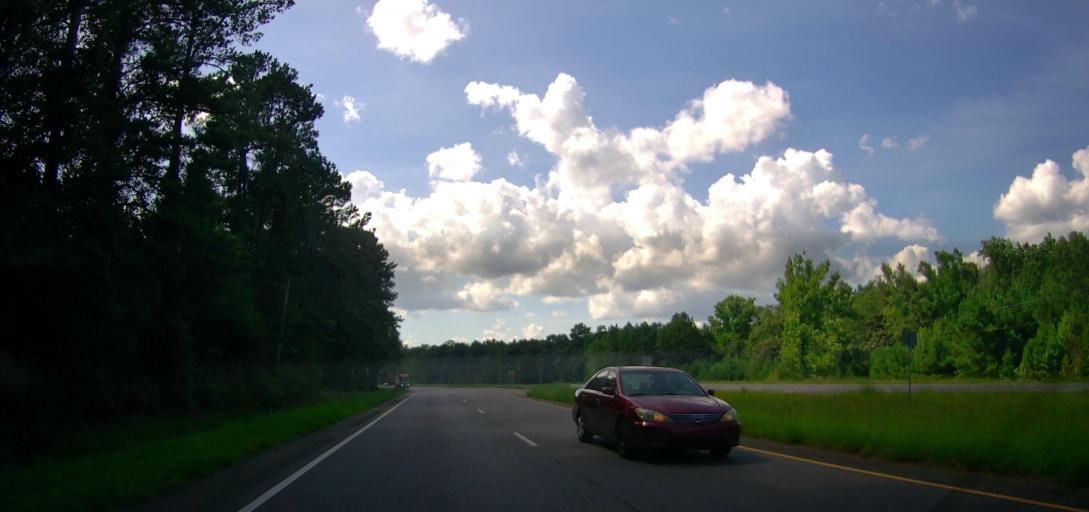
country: US
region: Alabama
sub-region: Pickens County
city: Reform
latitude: 33.3692
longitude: -87.9870
